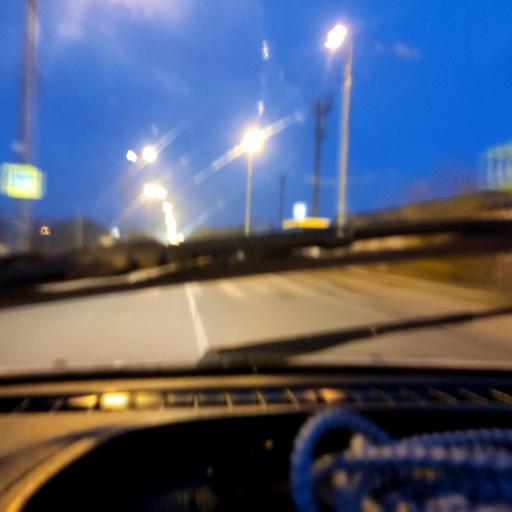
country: RU
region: Samara
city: Zhigulevsk
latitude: 53.4642
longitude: 49.5899
